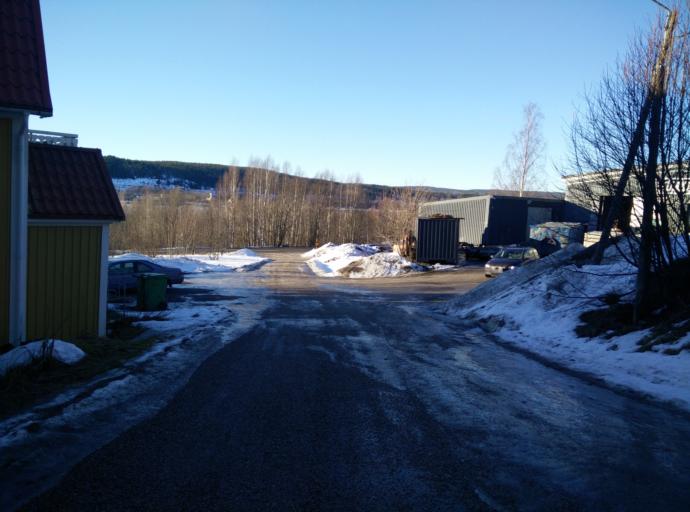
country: SE
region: Vaesternorrland
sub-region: Sundsvalls Kommun
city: Skottsund
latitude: 62.3143
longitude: 17.3946
